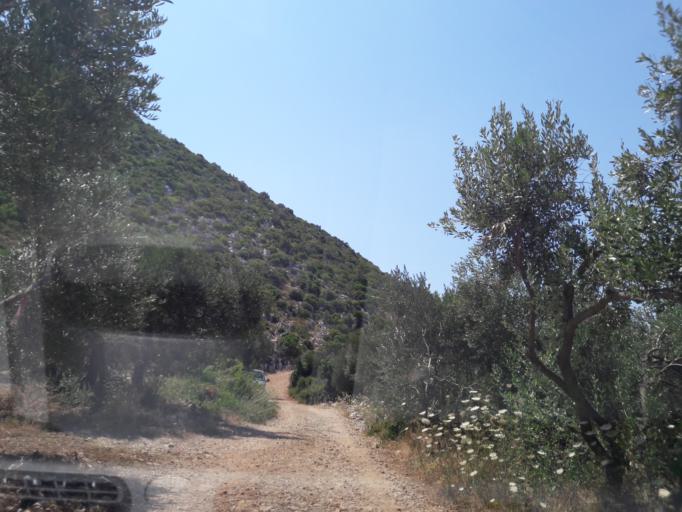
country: HR
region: Dubrovacko-Neretvanska
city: Orebic
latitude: 43.0215
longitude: 17.1665
